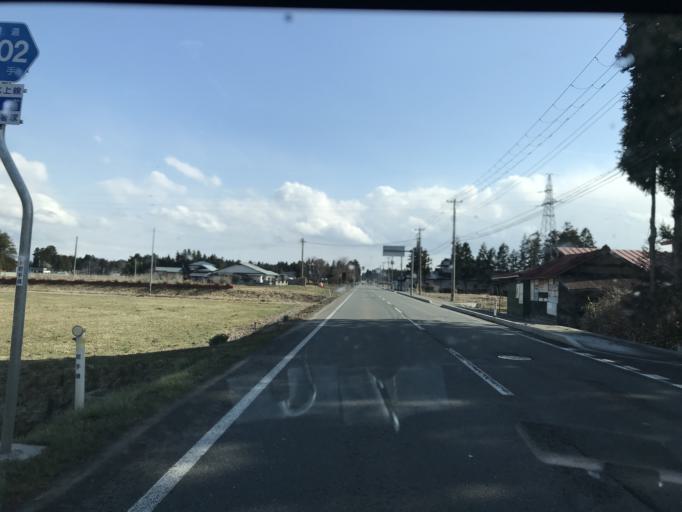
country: JP
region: Iwate
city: Mizusawa
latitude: 39.1284
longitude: 141.0531
